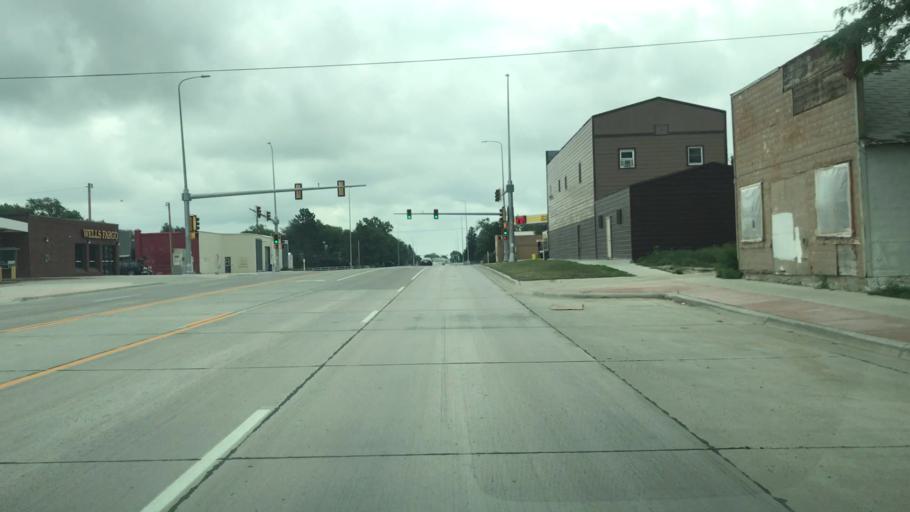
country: US
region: South Dakota
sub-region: Todd County
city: Mission
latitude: 43.3057
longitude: -100.6596
